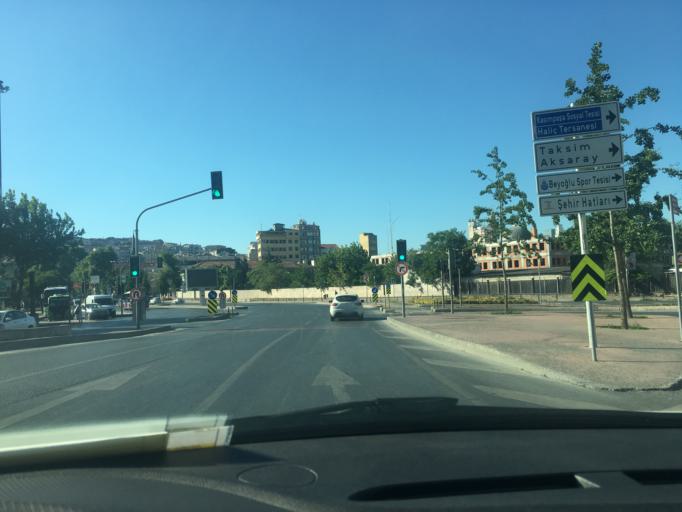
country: TR
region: Istanbul
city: Eminoenue
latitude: 41.0297
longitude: 28.9680
